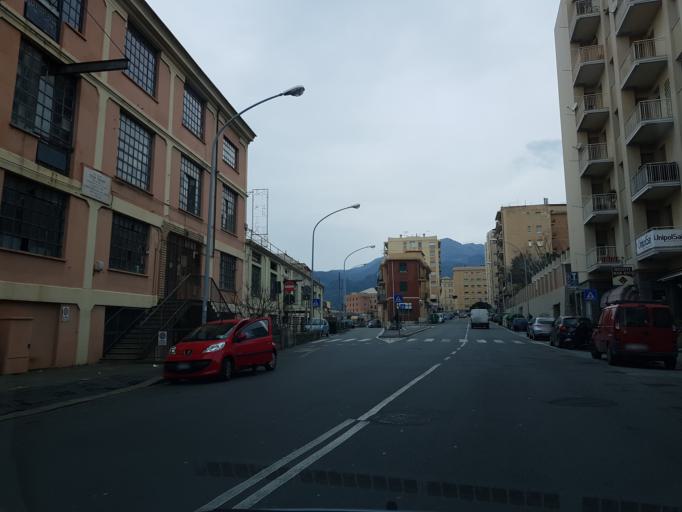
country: IT
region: Liguria
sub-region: Provincia di Genova
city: Mele
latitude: 44.4285
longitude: 8.7618
